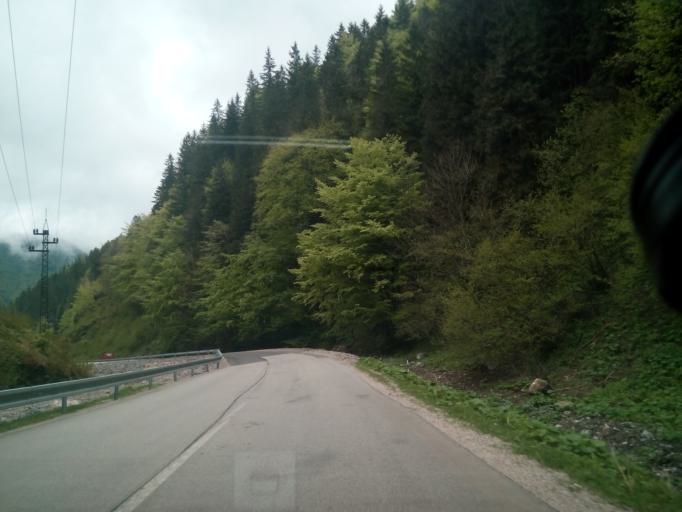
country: SK
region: Zilinsky
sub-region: Okres Zilina
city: Terchova
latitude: 49.2136
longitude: 19.0375
